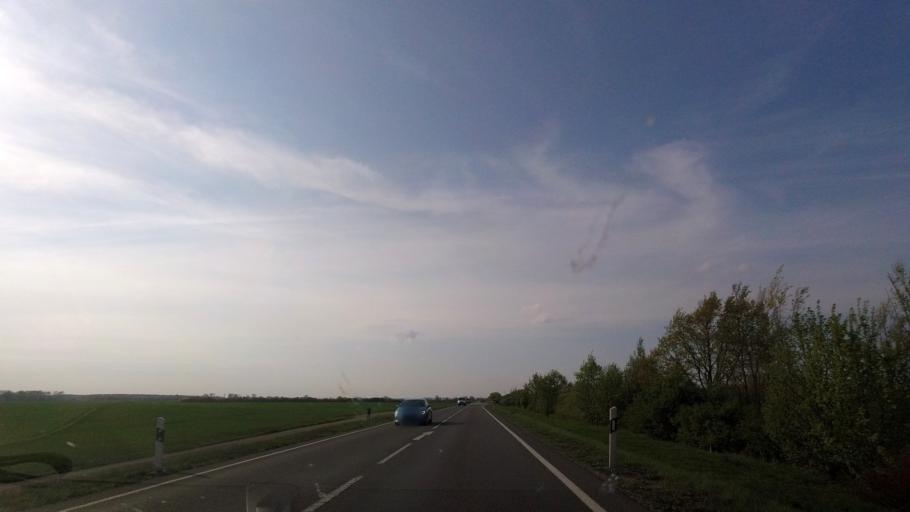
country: DE
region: Saxony-Anhalt
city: Wittenburg
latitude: 51.8292
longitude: 12.6355
